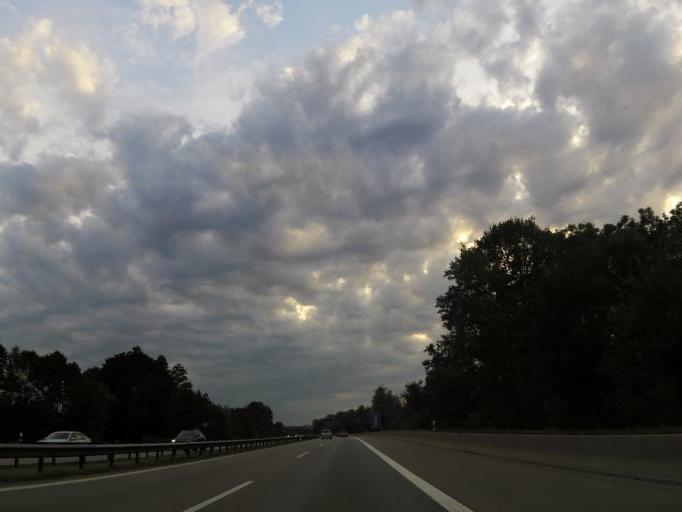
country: DE
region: Bavaria
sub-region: Upper Bavaria
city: Chiemsee
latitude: 47.8341
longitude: 12.4206
